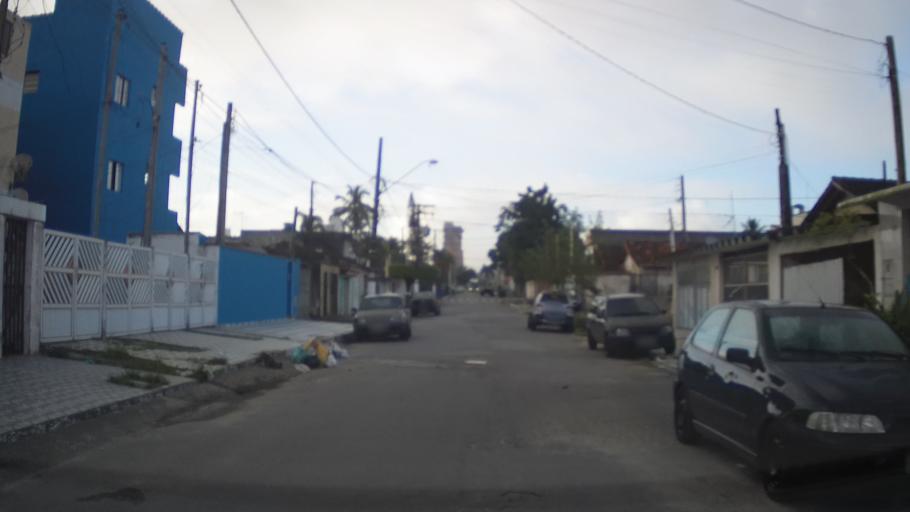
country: BR
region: Sao Paulo
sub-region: Praia Grande
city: Praia Grande
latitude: -24.0129
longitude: -46.4621
